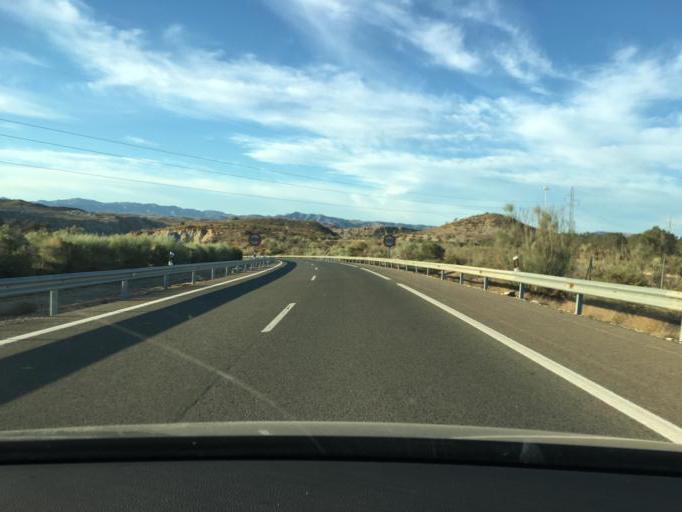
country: ES
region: Andalusia
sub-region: Provincia de Almeria
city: Sorbas
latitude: 37.0807
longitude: -2.0563
